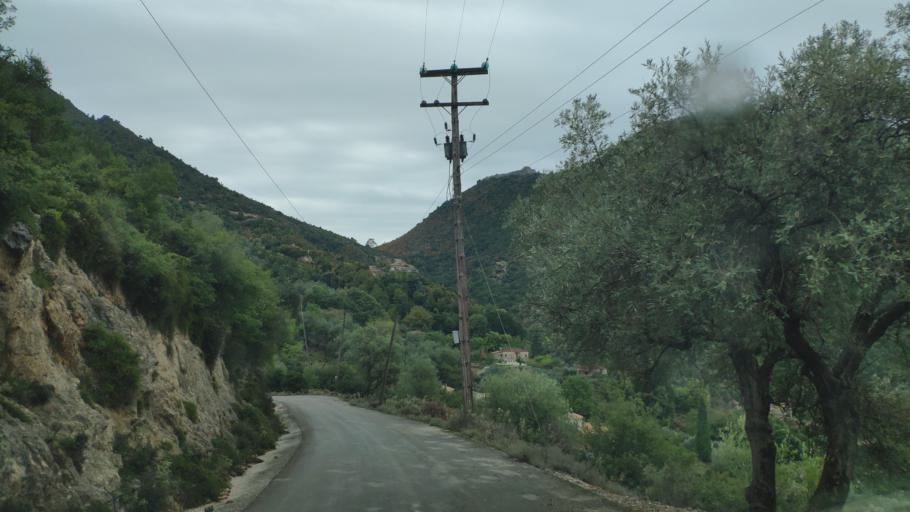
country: GR
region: Epirus
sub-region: Nomos Prevezis
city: Kanalaki
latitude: 39.3472
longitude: 20.6492
